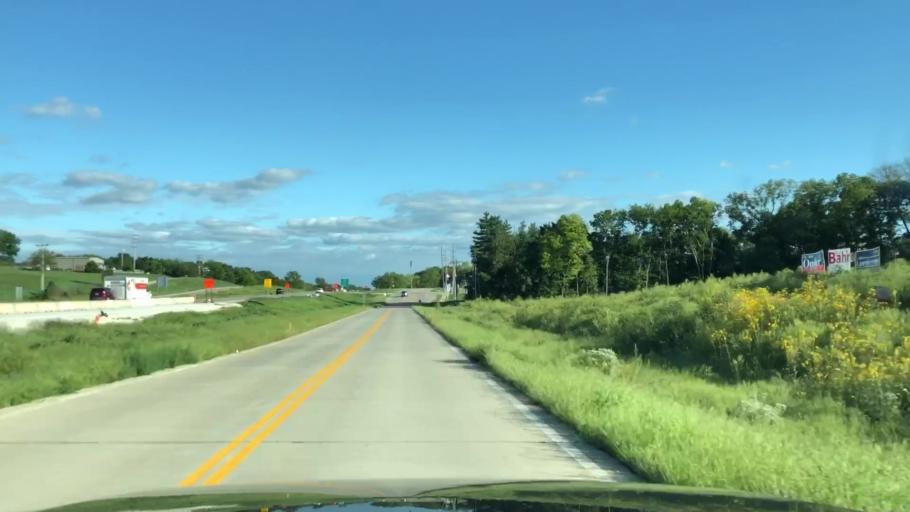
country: US
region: Missouri
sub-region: Saint Charles County
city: Wentzville
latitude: 38.8512
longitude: -90.8689
